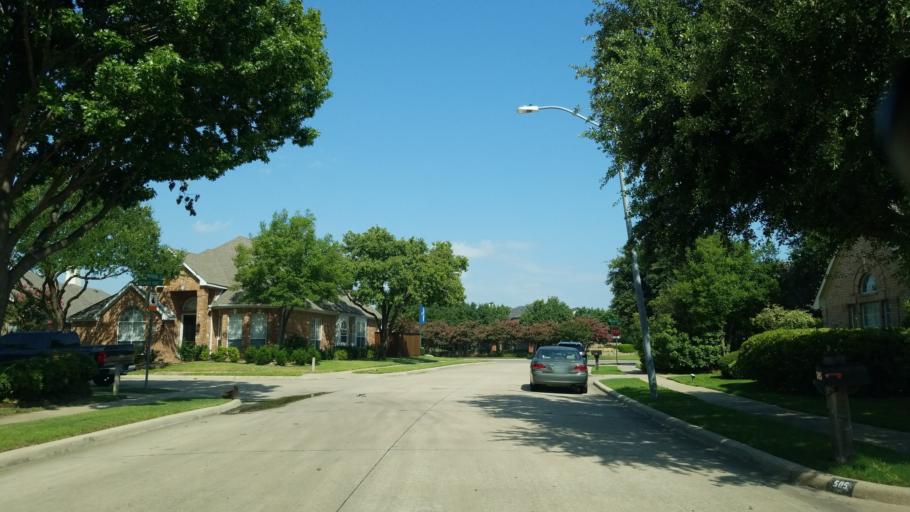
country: US
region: Texas
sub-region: Dallas County
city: Farmers Branch
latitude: 32.9247
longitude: -96.9526
